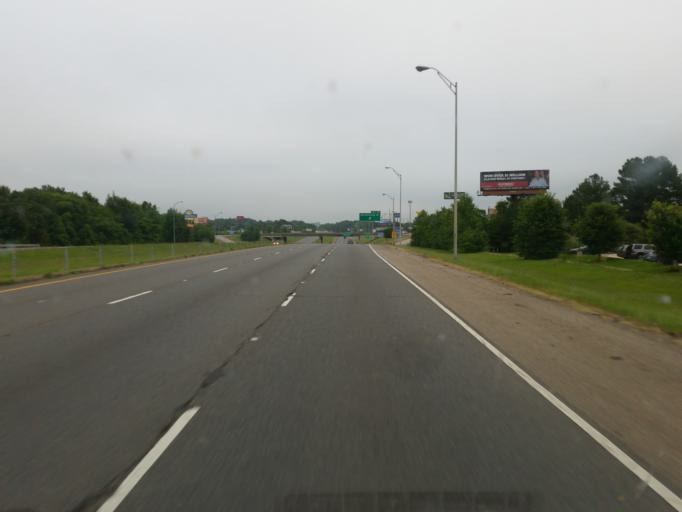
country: US
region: Louisiana
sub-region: Caddo Parish
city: Shreveport
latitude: 32.4599
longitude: -93.8323
